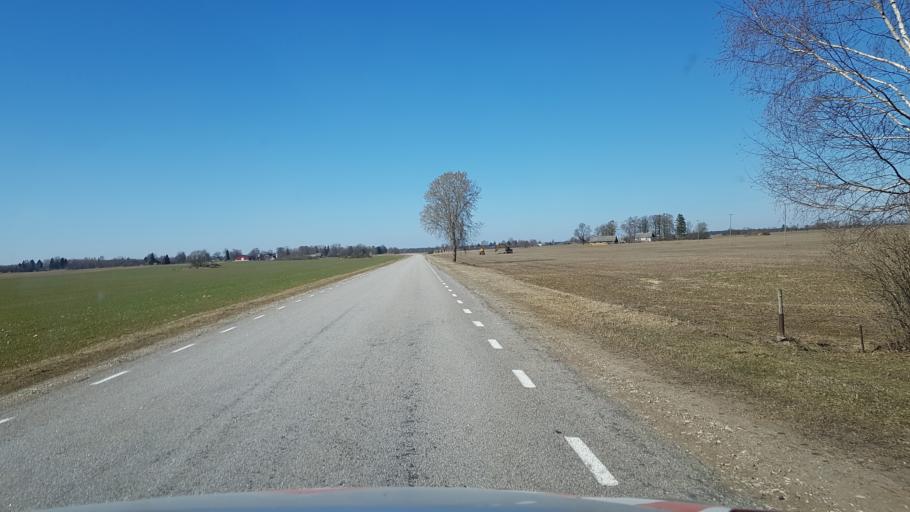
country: EE
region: Laeaene-Virumaa
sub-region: Vaeike-Maarja vald
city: Vaike-Maarja
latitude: 59.1011
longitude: 26.3936
